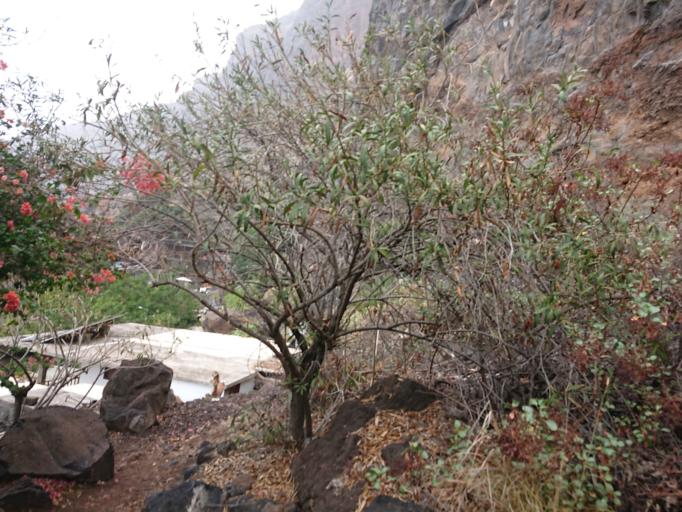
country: ES
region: Canary Islands
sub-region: Provincia de Santa Cruz de Tenerife
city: Tijarafe
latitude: 28.7216
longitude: -17.9791
